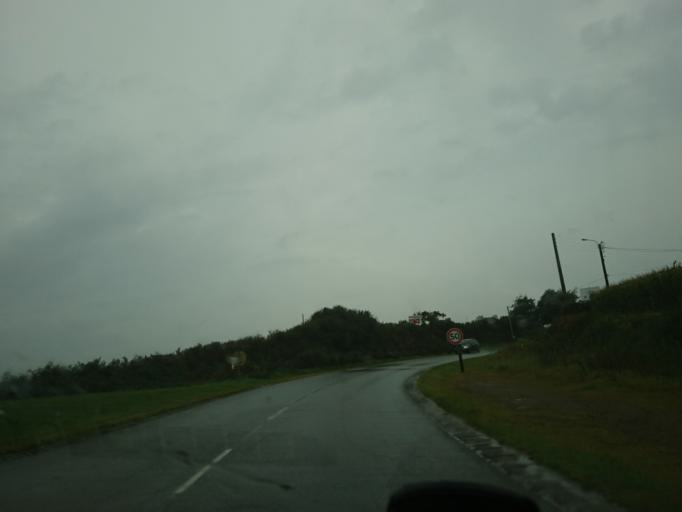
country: FR
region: Brittany
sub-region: Departement du Finistere
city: Plouguerneau
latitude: 48.6004
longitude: -4.5122
